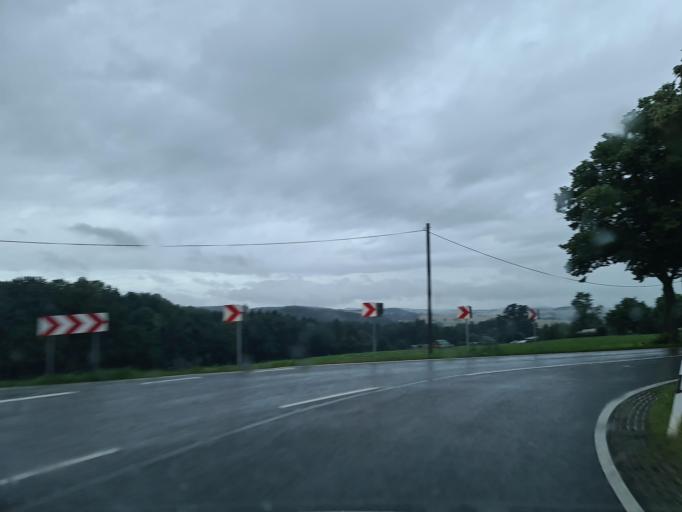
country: DE
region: Saxony
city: Neuensalz
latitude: 50.5269
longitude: 12.2500
